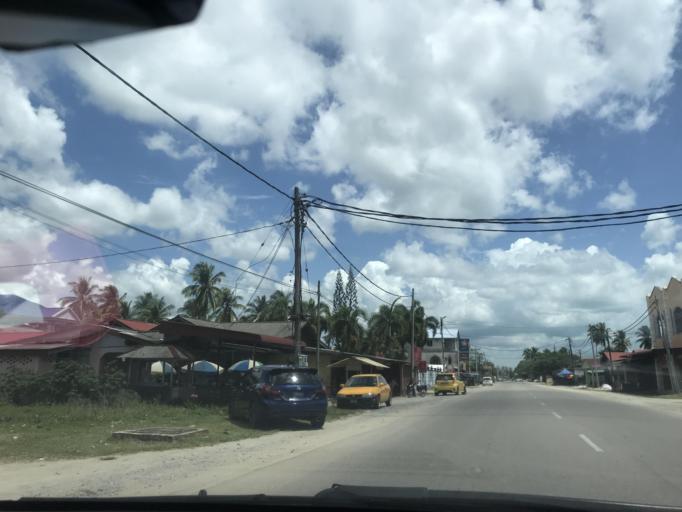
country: TH
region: Narathiwat
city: Tak Bai
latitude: 6.2259
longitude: 102.1028
